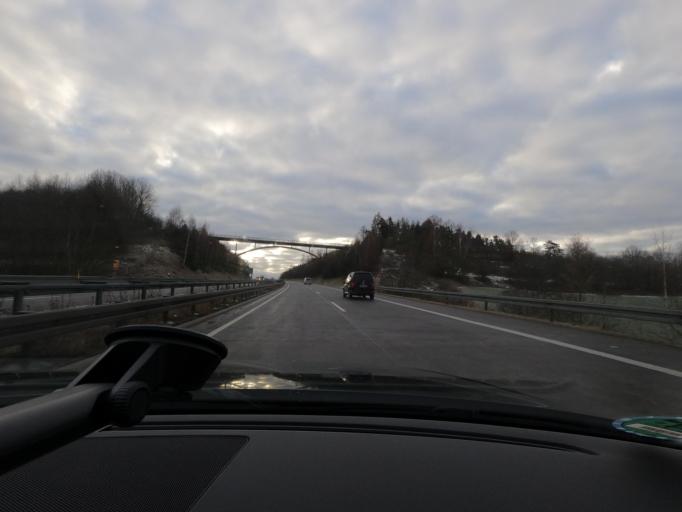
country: DE
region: Thuringia
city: Schleusingen
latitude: 50.5064
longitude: 10.7797
